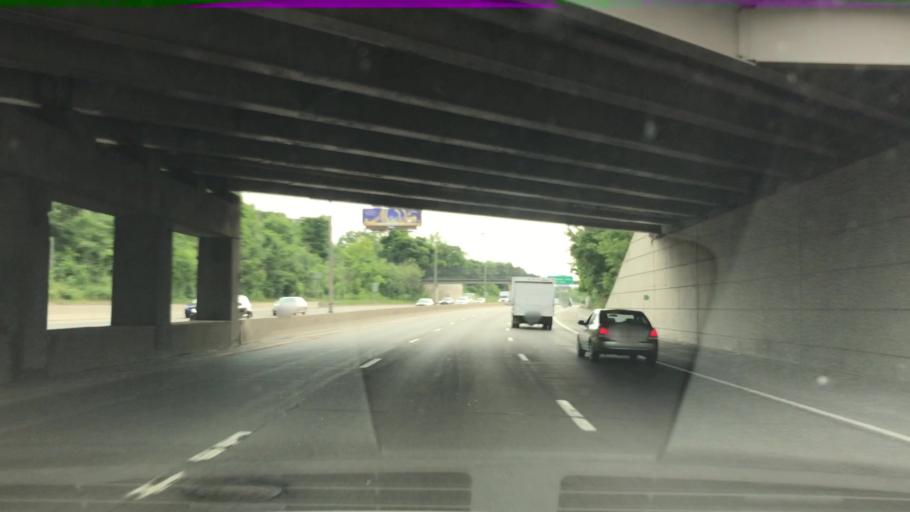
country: US
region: New York
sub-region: Erie County
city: Buffalo
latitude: 42.9002
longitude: -78.8488
